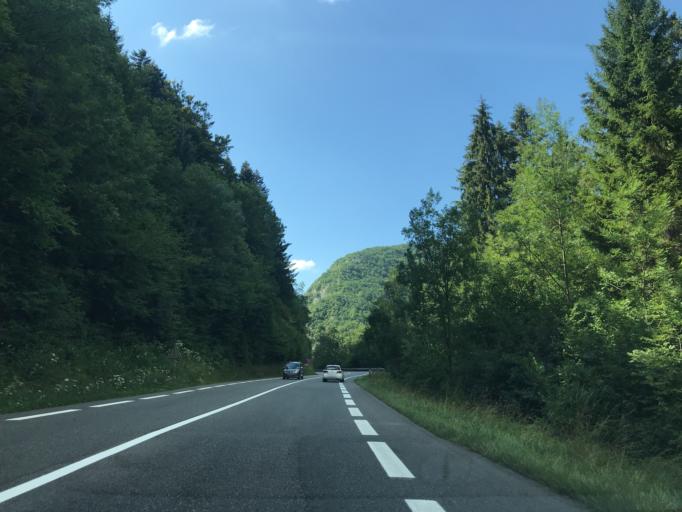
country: FR
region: Rhone-Alpes
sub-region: Departement de la Haute-Savoie
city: Dingy-Saint-Clair
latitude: 45.8992
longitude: 6.2135
